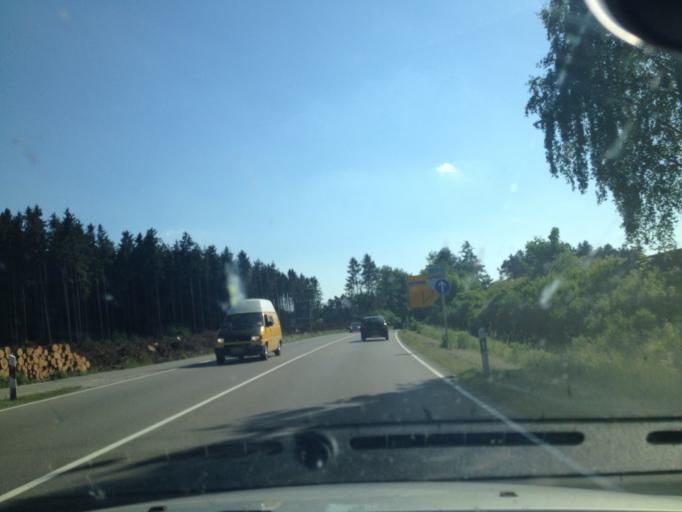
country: DE
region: Bavaria
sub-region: Swabia
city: Obergriesbach
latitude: 48.4012
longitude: 11.0818
